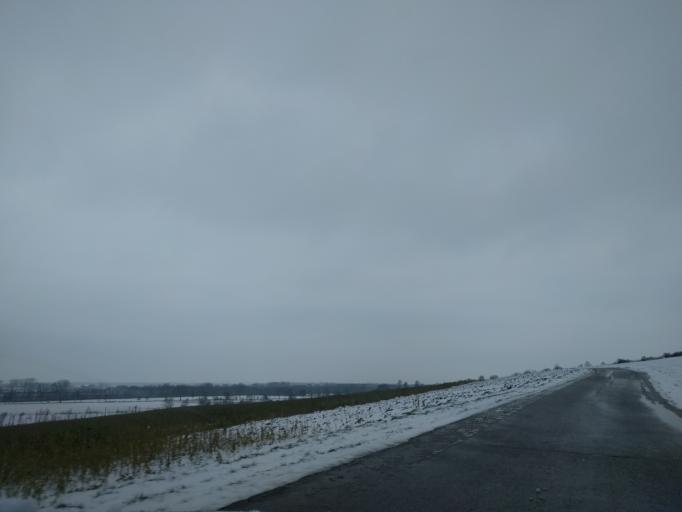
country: DE
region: Bavaria
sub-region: Swabia
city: Tapfheim
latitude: 48.6946
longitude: 10.7293
